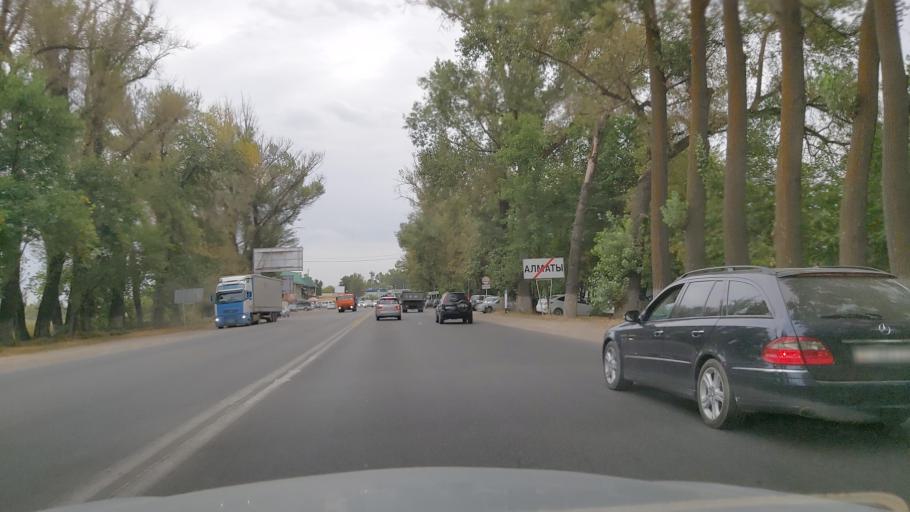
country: KZ
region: Almaty Oblysy
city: Energeticheskiy
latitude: 43.3351
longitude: 77.0387
